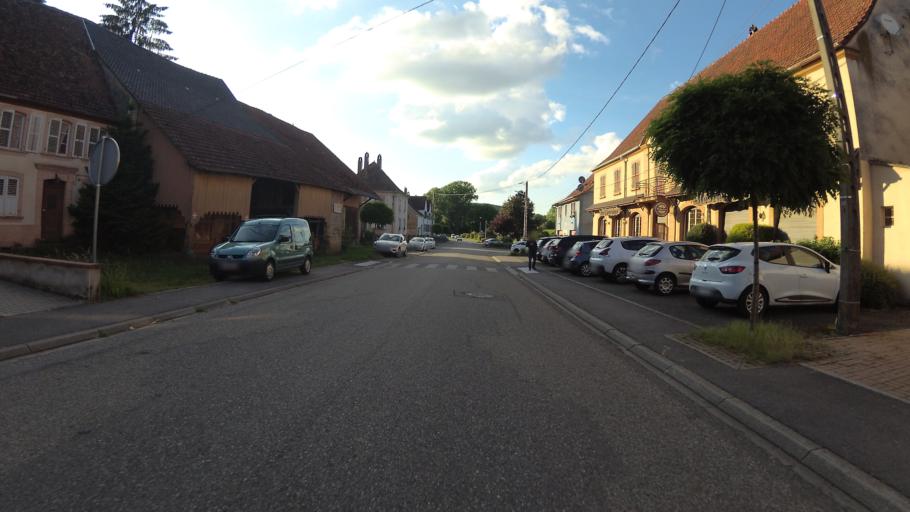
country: FR
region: Alsace
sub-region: Departement du Bas-Rhin
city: Oermingen
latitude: 48.9636
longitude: 7.1401
